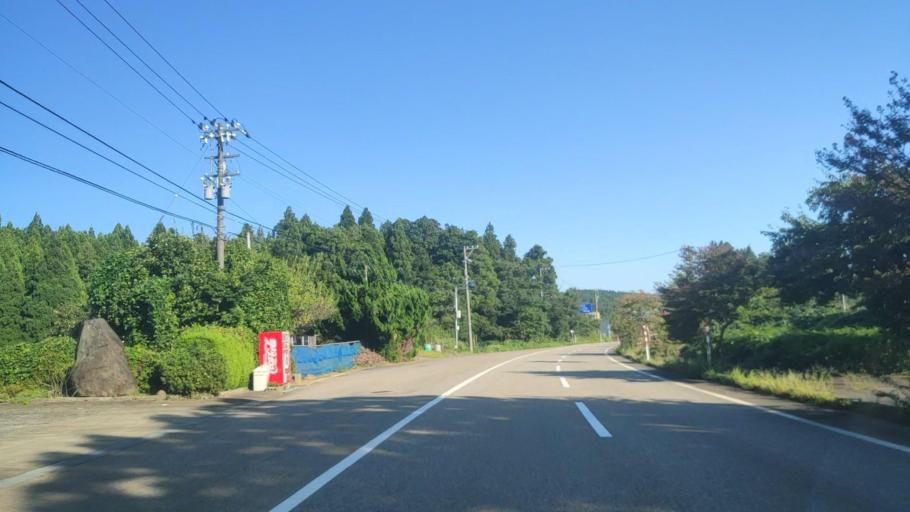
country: JP
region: Ishikawa
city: Nanao
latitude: 37.1248
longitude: 136.9281
